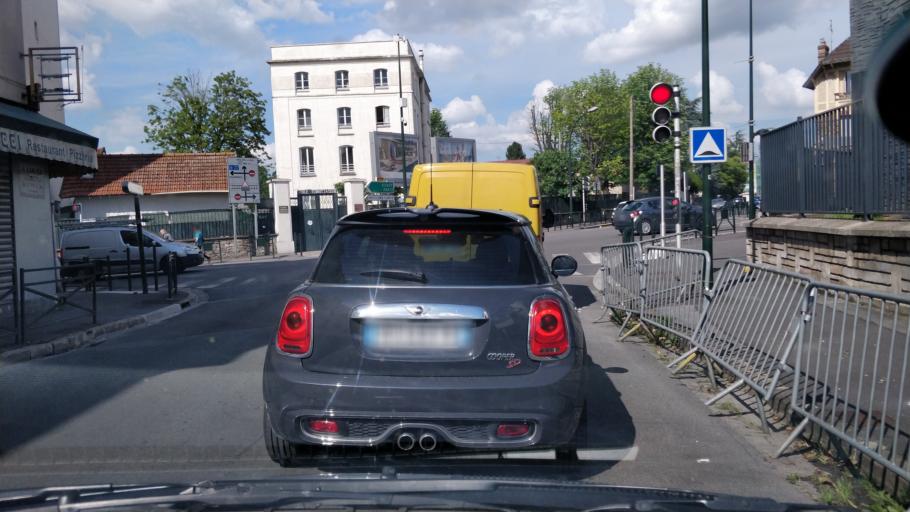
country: FR
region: Ile-de-France
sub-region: Departement de Seine-Saint-Denis
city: Le Raincy
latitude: 48.9011
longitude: 2.5120
